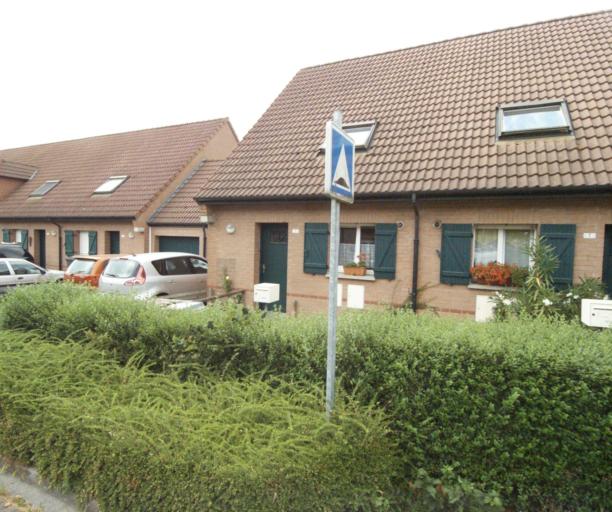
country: FR
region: Nord-Pas-de-Calais
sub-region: Departement du Nord
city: Neuville-en-Ferrain
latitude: 50.7517
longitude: 3.1515
